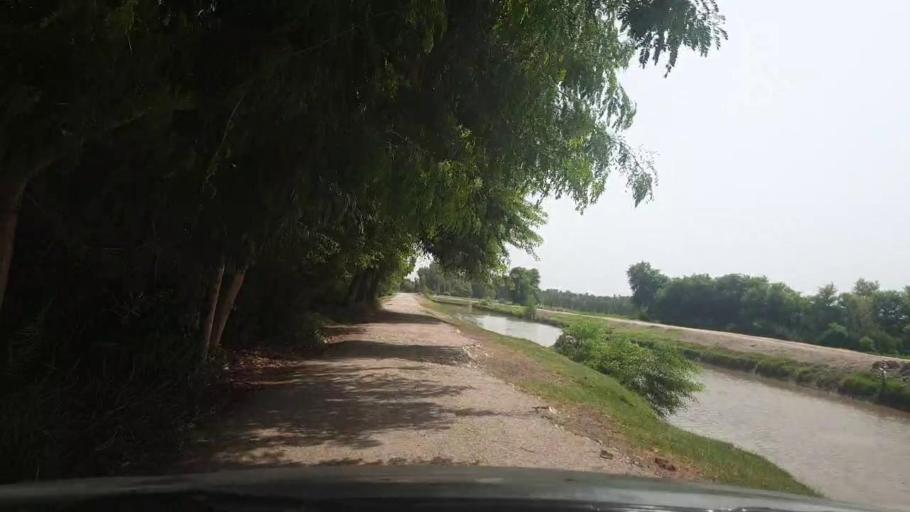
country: PK
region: Sindh
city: Pano Aqil
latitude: 27.8817
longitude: 69.1234
